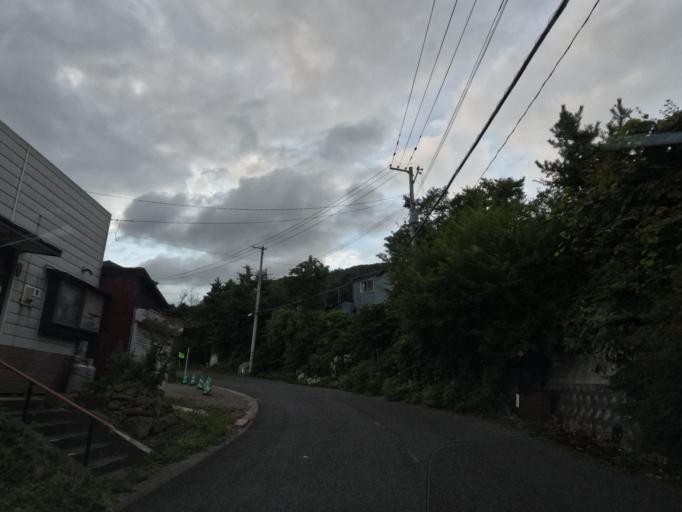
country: JP
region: Hokkaido
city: Muroran
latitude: 42.3623
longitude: 140.9679
